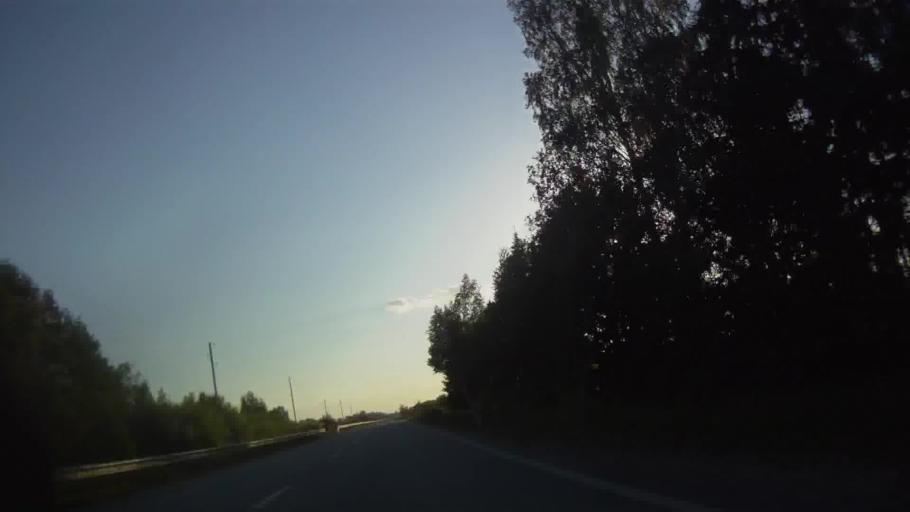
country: LV
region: Livani
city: Livani
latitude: 56.5343
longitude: 26.2907
